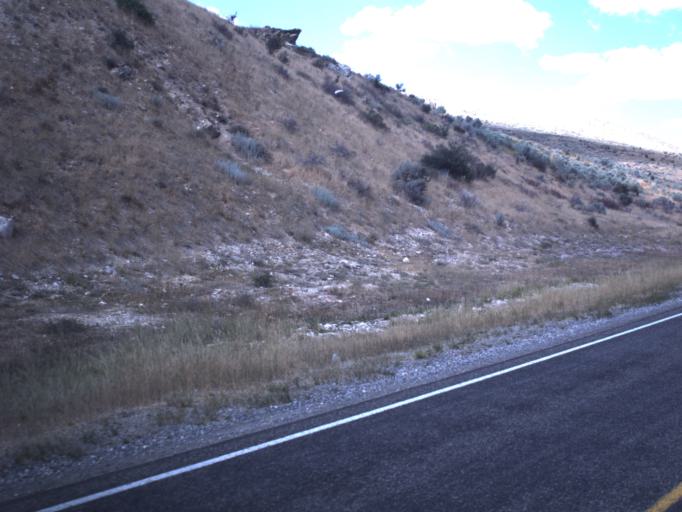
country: US
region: Utah
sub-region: Rich County
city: Randolph
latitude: 41.8654
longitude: -111.3646
